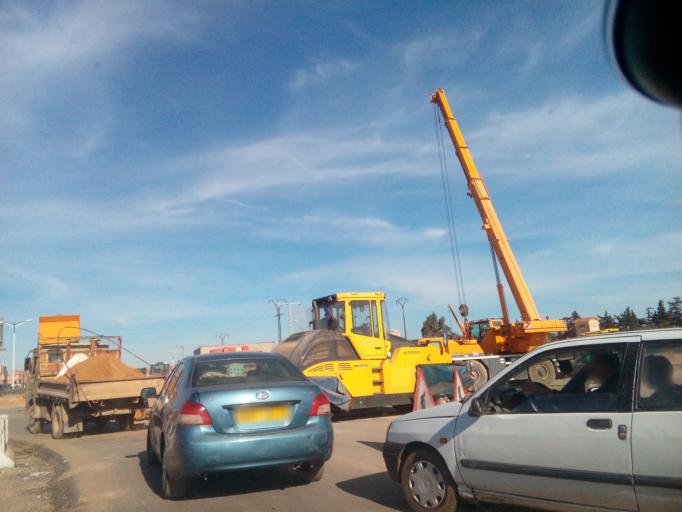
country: DZ
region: Mostaganem
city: Mostaganem
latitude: 35.9318
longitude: 0.1197
